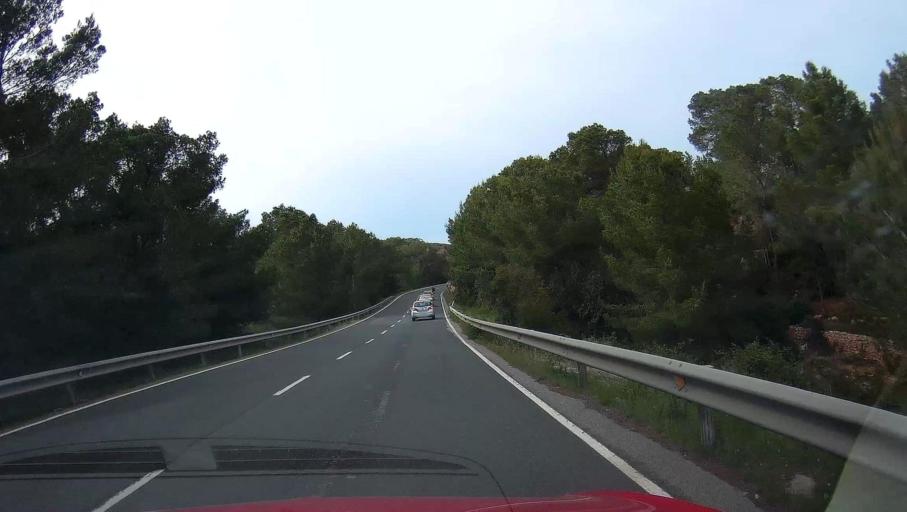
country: ES
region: Balearic Islands
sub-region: Illes Balears
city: Sant Joan de Labritja
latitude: 39.0943
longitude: 1.4989
